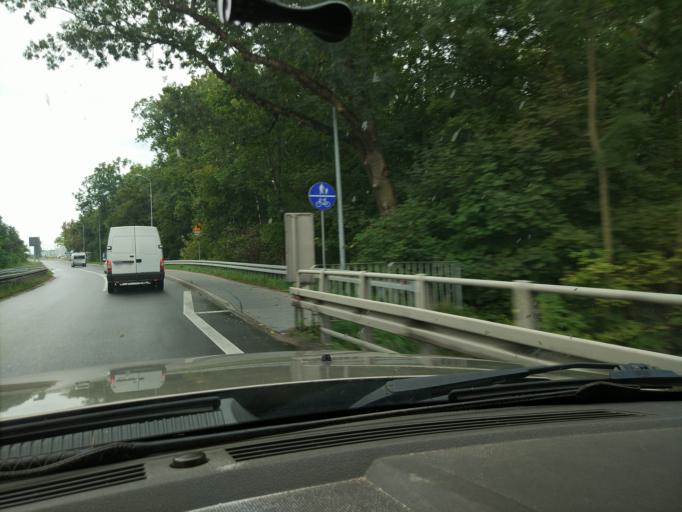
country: PL
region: Masovian Voivodeship
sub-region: Powiat pruszkowski
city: Brwinow
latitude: 52.1835
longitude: 20.7502
